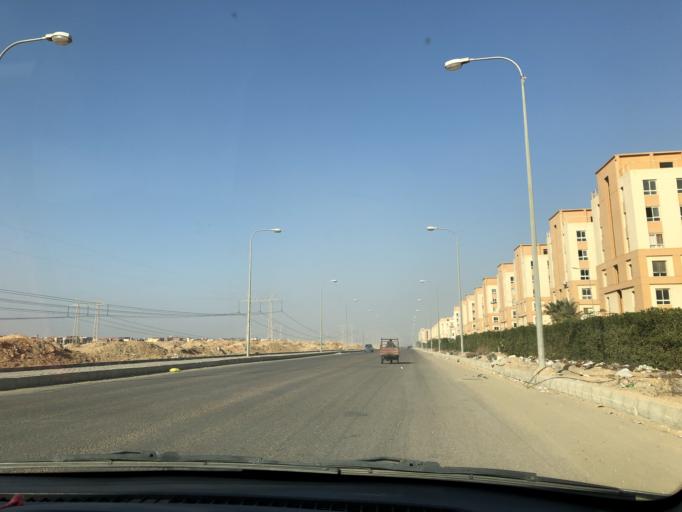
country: EG
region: Al Jizah
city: Madinat Sittah Uktubar
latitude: 29.9082
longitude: 31.0513
